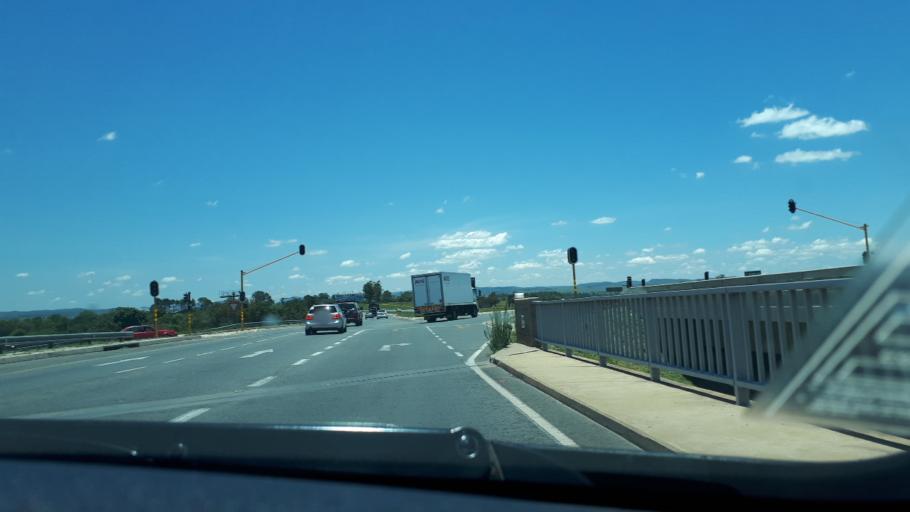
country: ZA
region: Gauteng
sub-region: City of Johannesburg Metropolitan Municipality
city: Diepsloot
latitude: -25.9831
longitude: 27.9254
